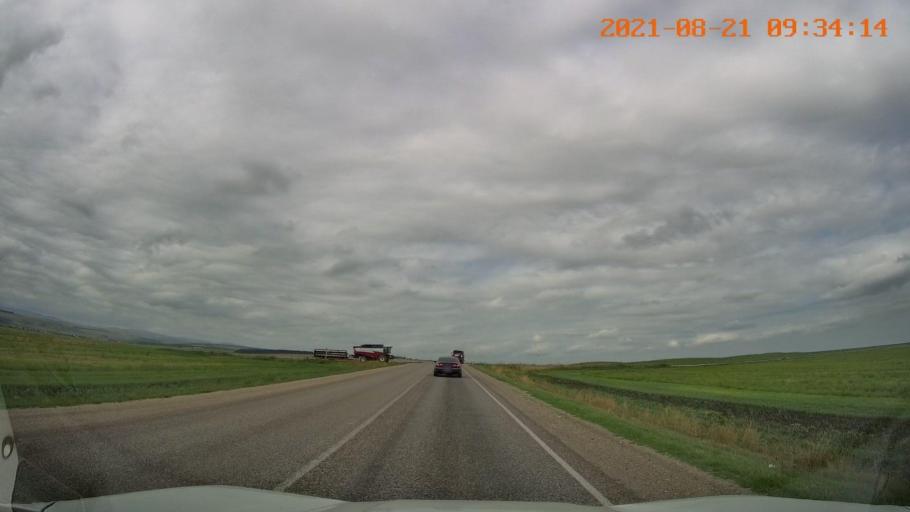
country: RU
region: Stavropol'skiy
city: Yutsa
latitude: 43.9926
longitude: 42.9752
